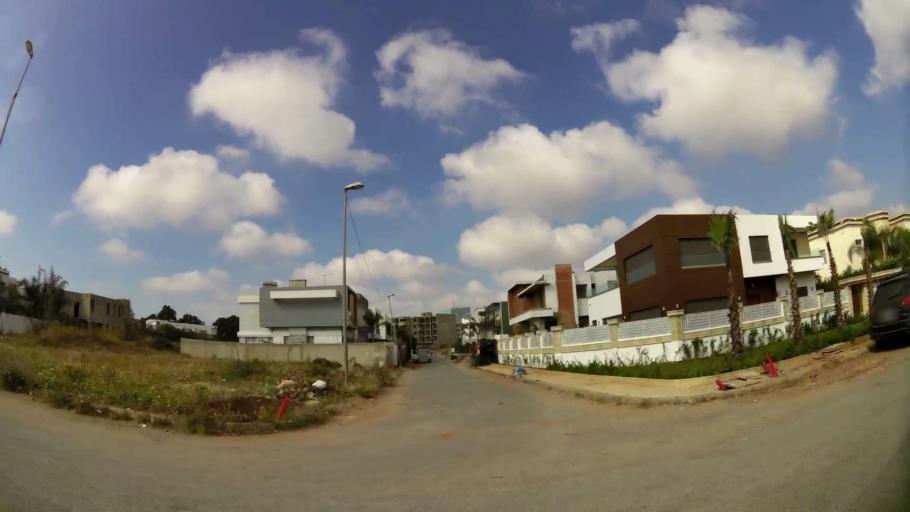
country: MA
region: Rabat-Sale-Zemmour-Zaer
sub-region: Skhirate-Temara
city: Temara
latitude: 33.9521
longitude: -6.8780
